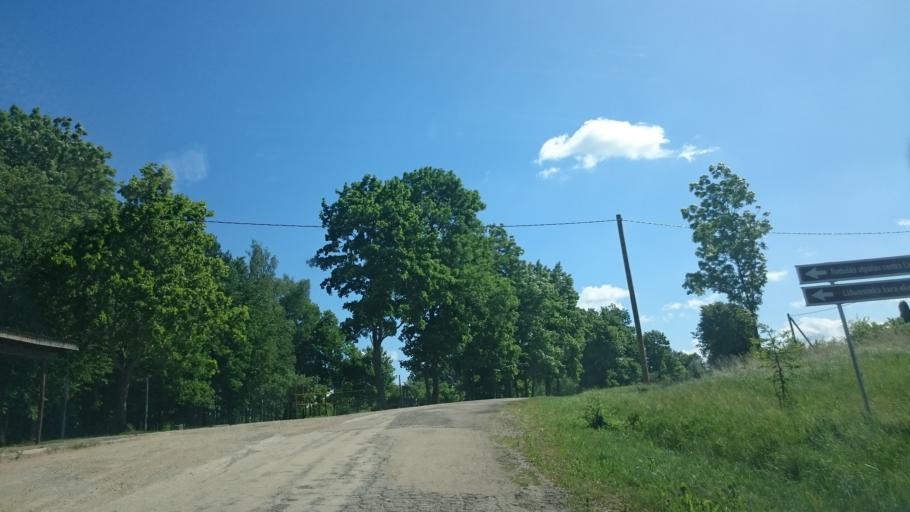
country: LV
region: Cibla
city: Cibla
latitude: 56.5928
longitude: 27.9896
